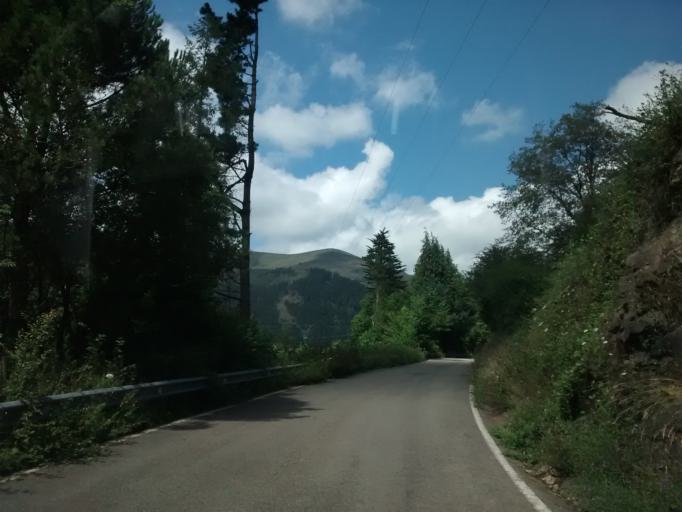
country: ES
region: Cantabria
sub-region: Provincia de Cantabria
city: Ruente
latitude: 43.1979
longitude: -4.2942
